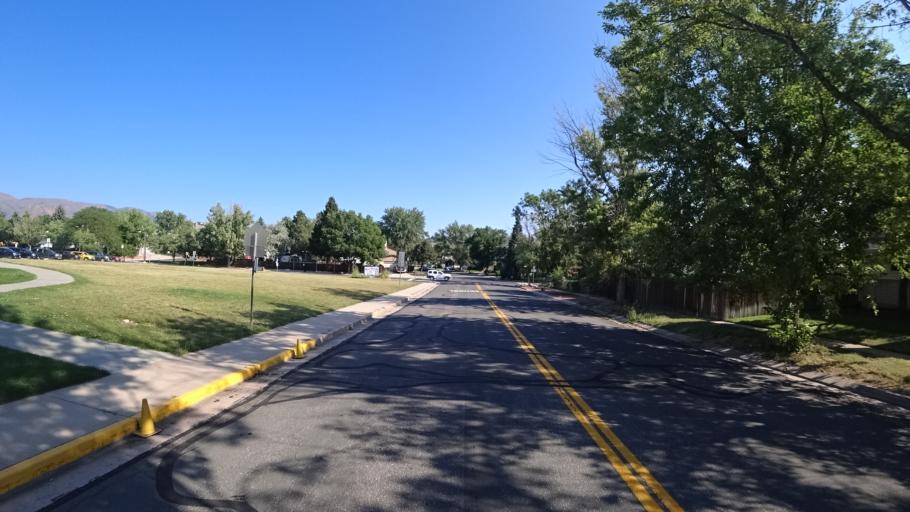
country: US
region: Colorado
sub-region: El Paso County
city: Colorado Springs
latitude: 38.8925
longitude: -104.8387
